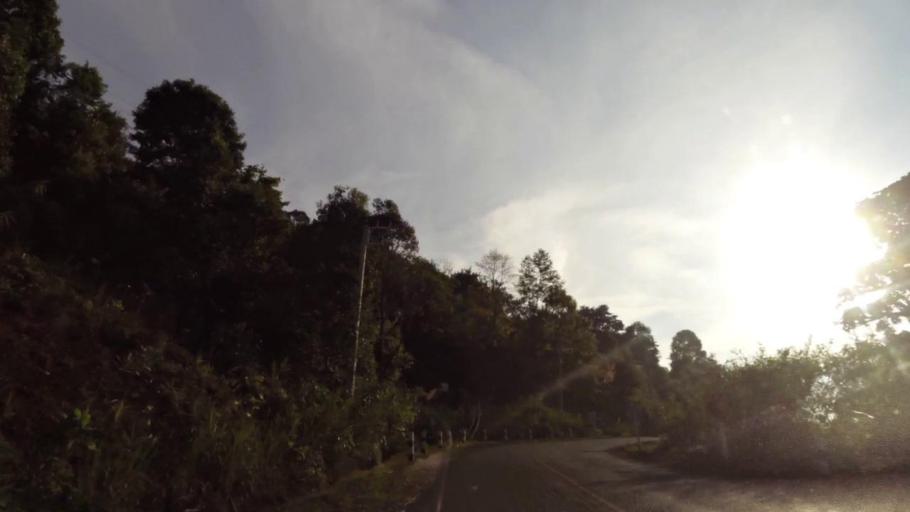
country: TH
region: Chiang Rai
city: Khun Tan
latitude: 19.8602
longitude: 100.4358
